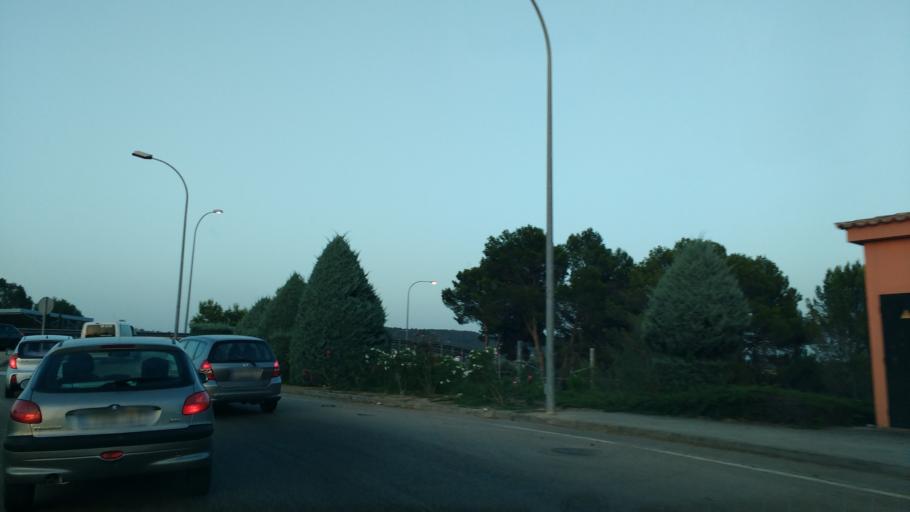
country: ES
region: Balearic Islands
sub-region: Illes Balears
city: Marratxi
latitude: 39.6315
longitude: 2.7354
